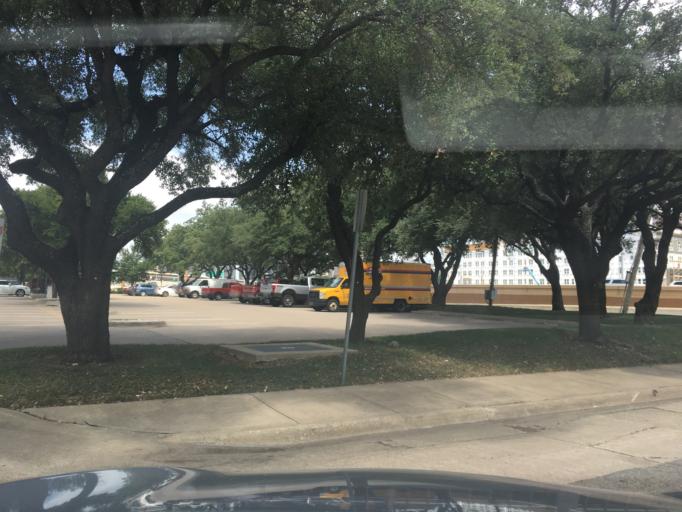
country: US
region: Texas
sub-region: Dallas County
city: Addison
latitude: 32.9244
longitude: -96.8150
